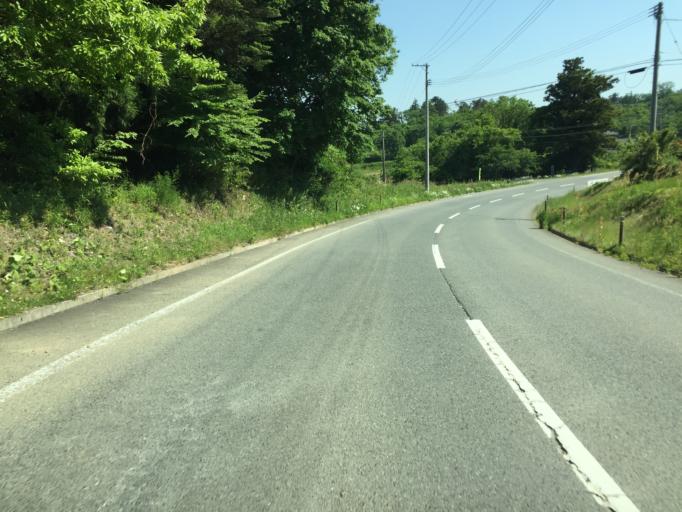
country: JP
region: Miyagi
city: Marumori
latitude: 37.8143
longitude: 140.8833
